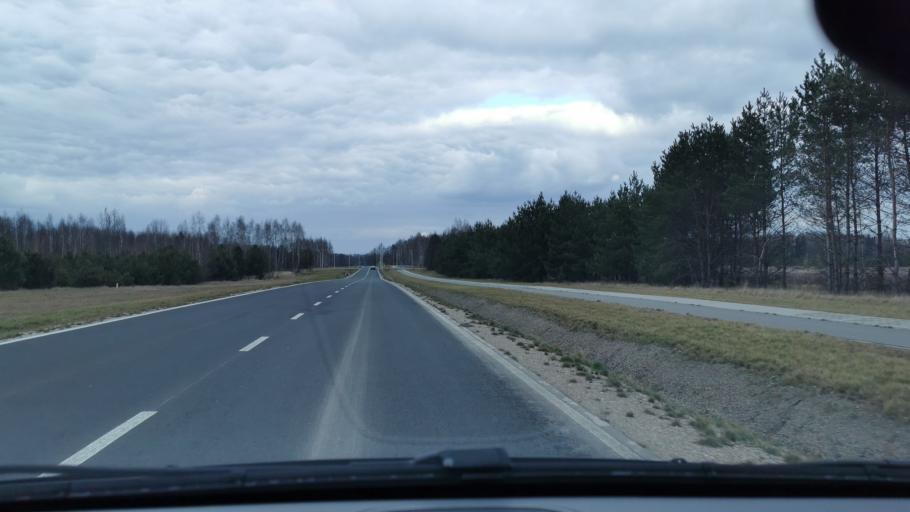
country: PL
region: Masovian Voivodeship
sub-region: Powiat zyrardowski
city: Zyrardow
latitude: 51.9996
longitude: 20.4638
